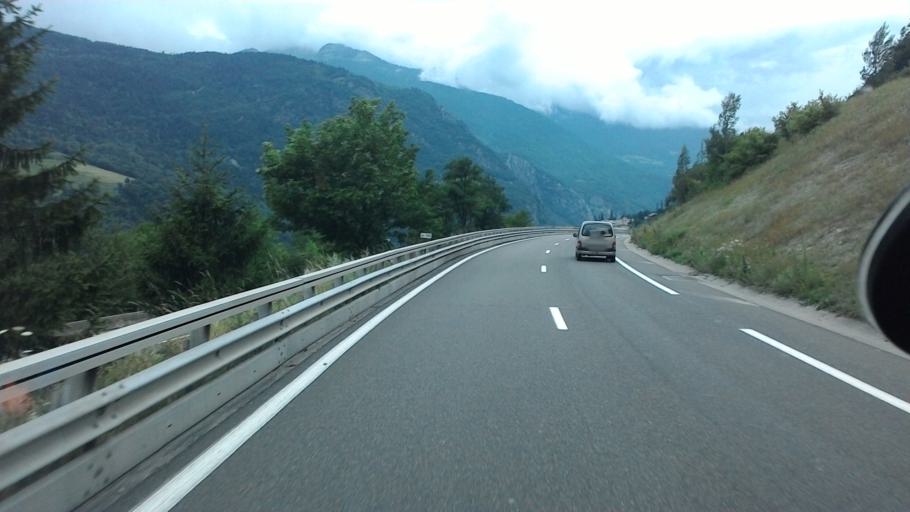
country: FR
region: Rhone-Alpes
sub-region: Departement de la Savoie
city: Aigueblanche
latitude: 45.5088
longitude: 6.5035
